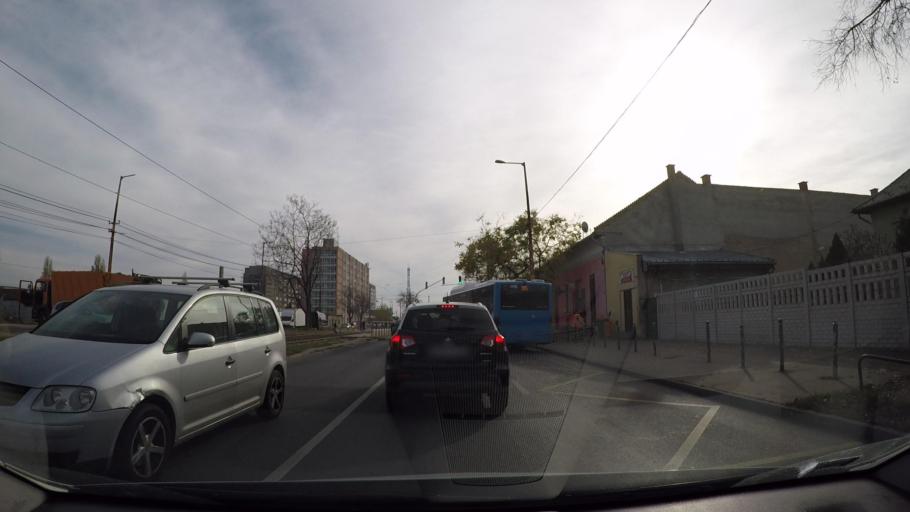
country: HU
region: Budapest
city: Budapest X. keruelet
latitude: 47.4779
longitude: 19.1650
